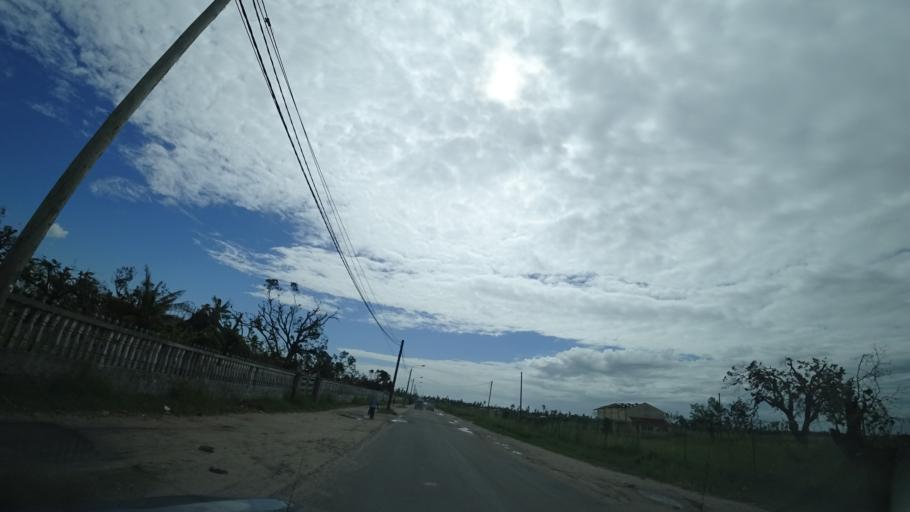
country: MZ
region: Sofala
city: Beira
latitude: -19.7954
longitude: 34.8920
